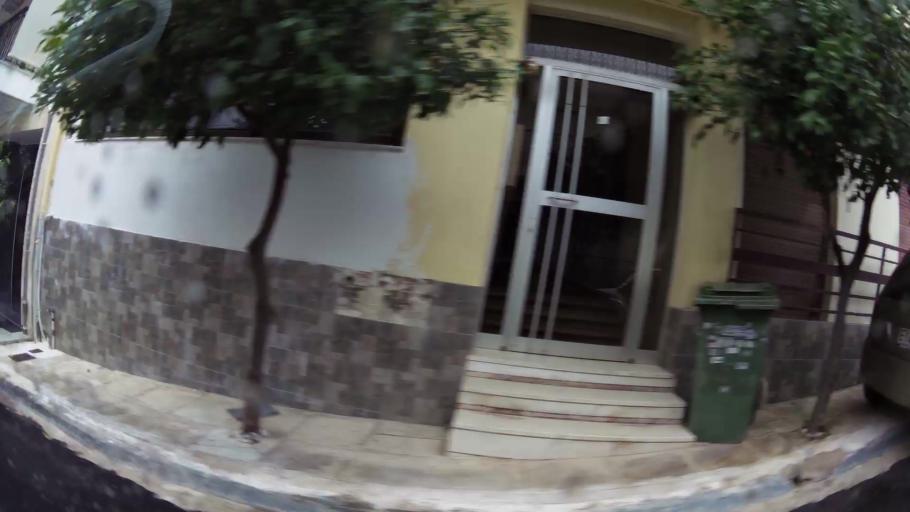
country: GR
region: Attica
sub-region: Nomos Piraios
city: Korydallos
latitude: 37.9971
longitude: 23.6408
